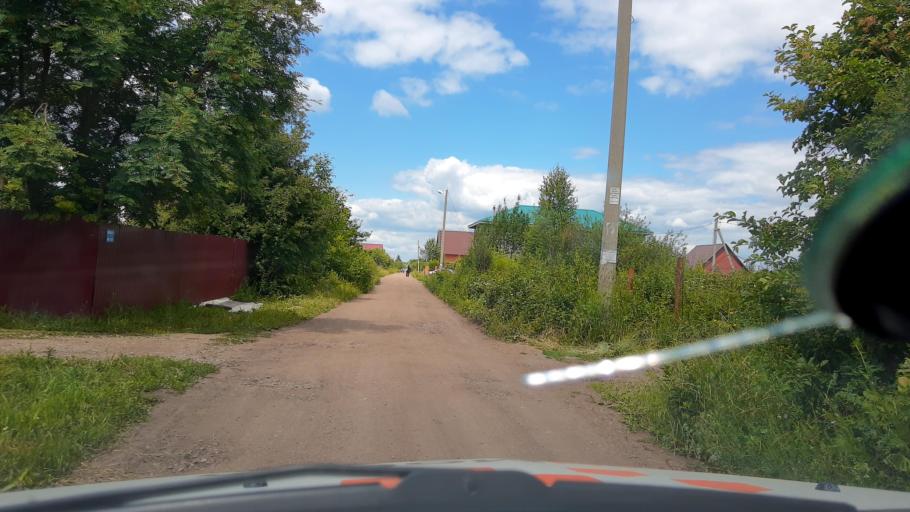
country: RU
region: Bashkortostan
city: Kabakovo
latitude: 54.7203
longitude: 56.2092
